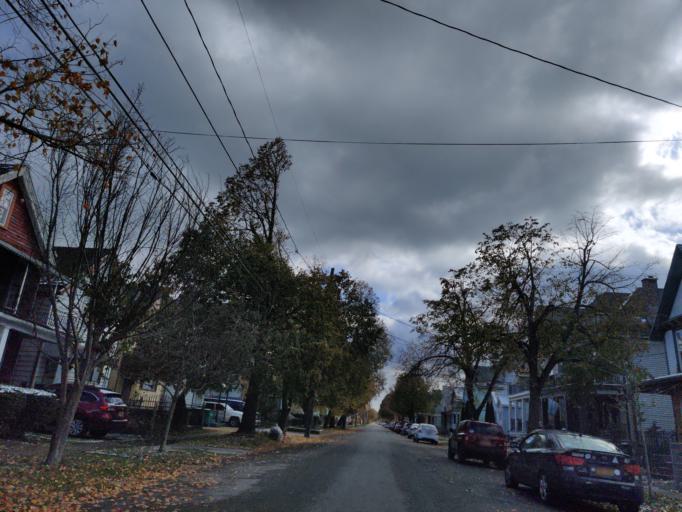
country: US
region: New York
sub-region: Erie County
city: Buffalo
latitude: 42.9086
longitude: -78.8906
